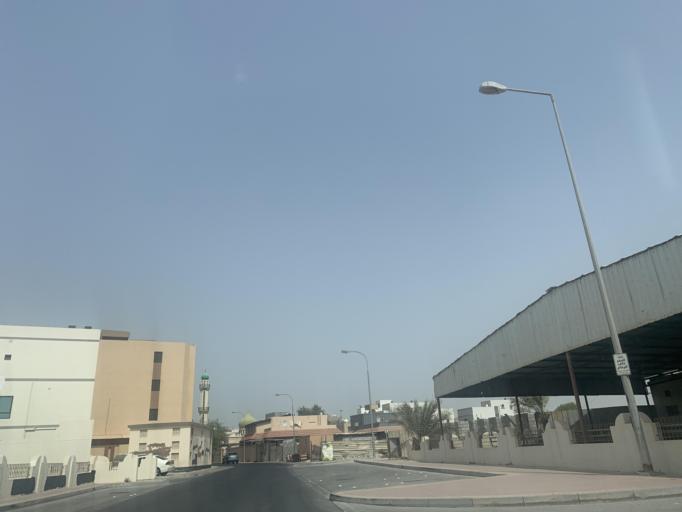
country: BH
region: Manama
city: Jidd Hafs
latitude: 26.2136
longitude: 50.4624
